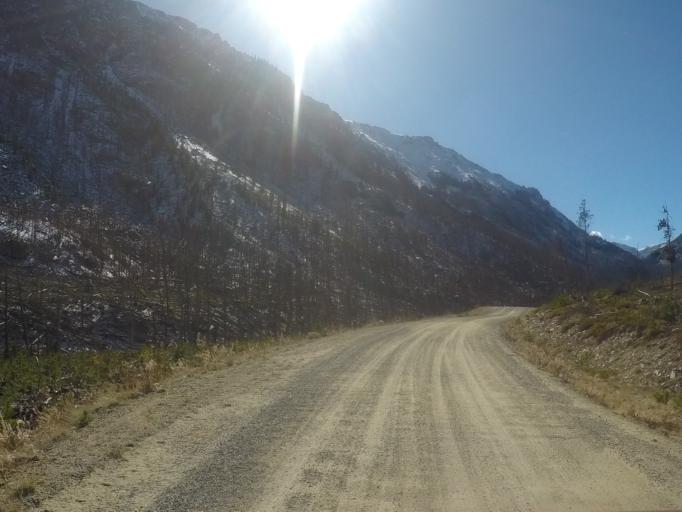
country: US
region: Montana
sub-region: Carbon County
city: Red Lodge
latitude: 45.1690
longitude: -109.4913
